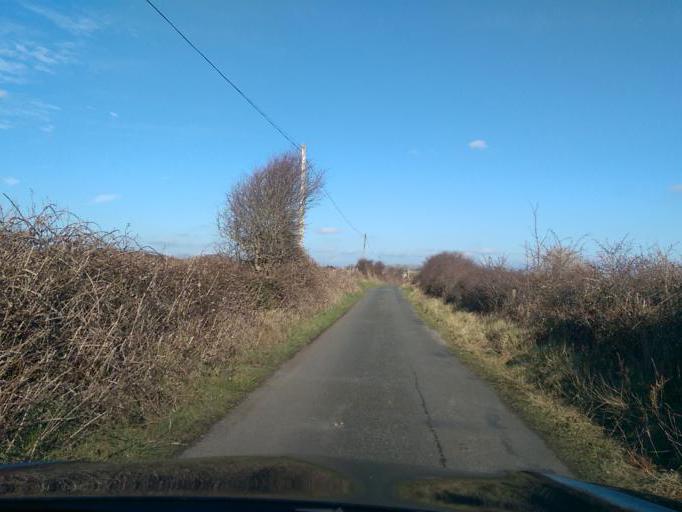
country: IE
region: Connaught
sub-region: County Galway
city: Oranmore
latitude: 53.2370
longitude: -8.9699
